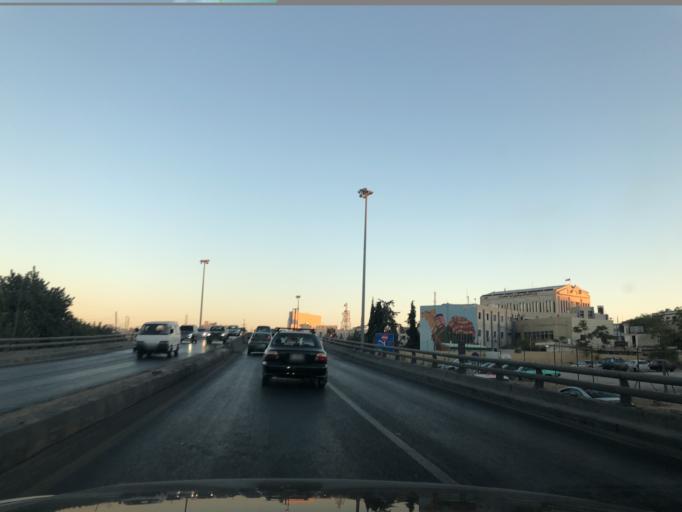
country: JO
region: Amman
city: Wadi as Sir
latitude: 31.9583
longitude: 35.8462
